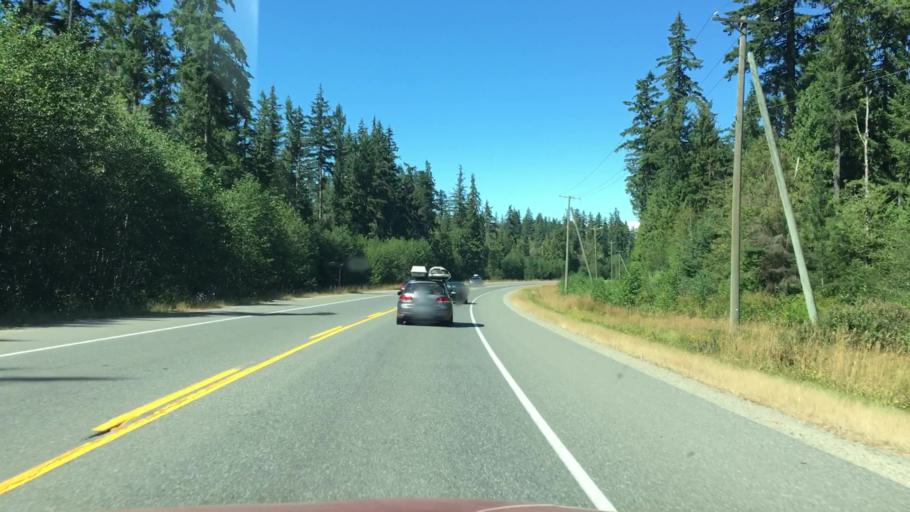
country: CA
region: British Columbia
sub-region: Regional District of Nanaimo
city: Parksville
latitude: 49.3095
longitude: -124.4500
